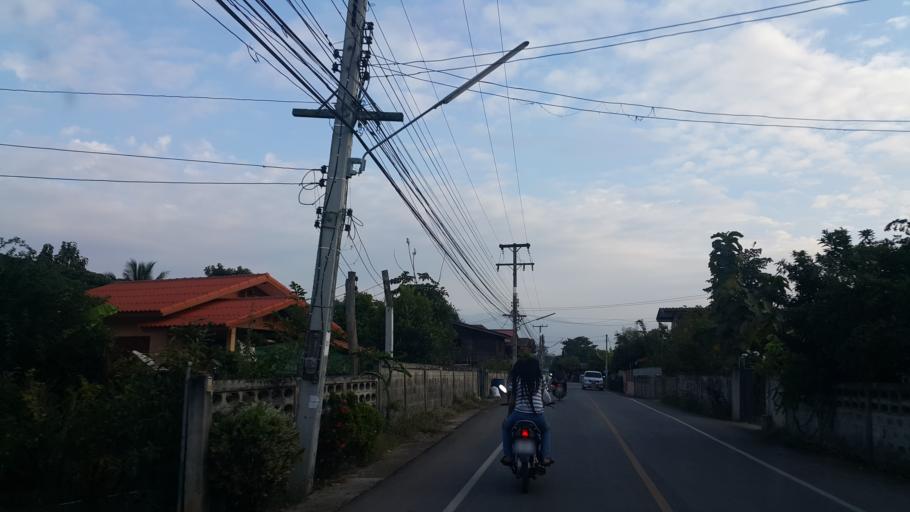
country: TH
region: Lampang
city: Sop Prap
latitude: 17.8915
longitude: 99.3324
